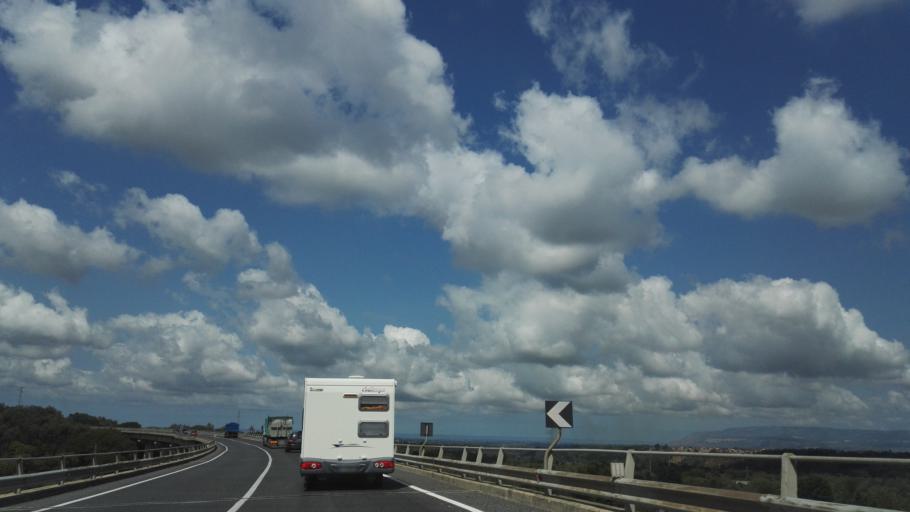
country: IT
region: Calabria
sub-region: Provincia di Reggio Calabria
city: Anoia Superiore
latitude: 38.4213
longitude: 16.0975
